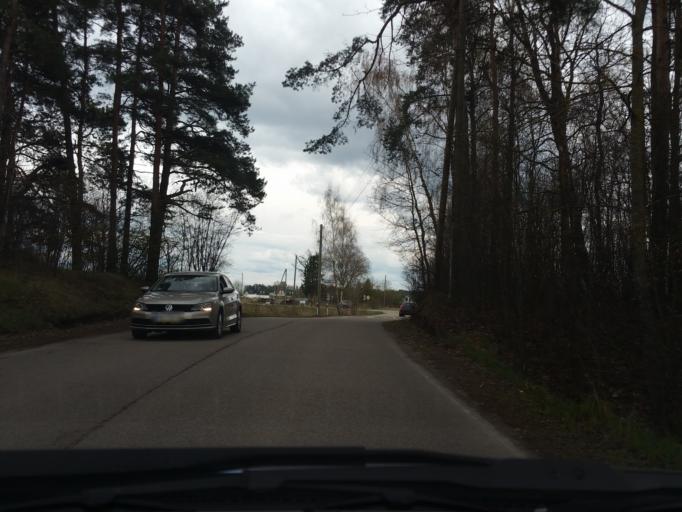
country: LV
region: Marupe
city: Marupe
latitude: 56.9214
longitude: 23.9986
